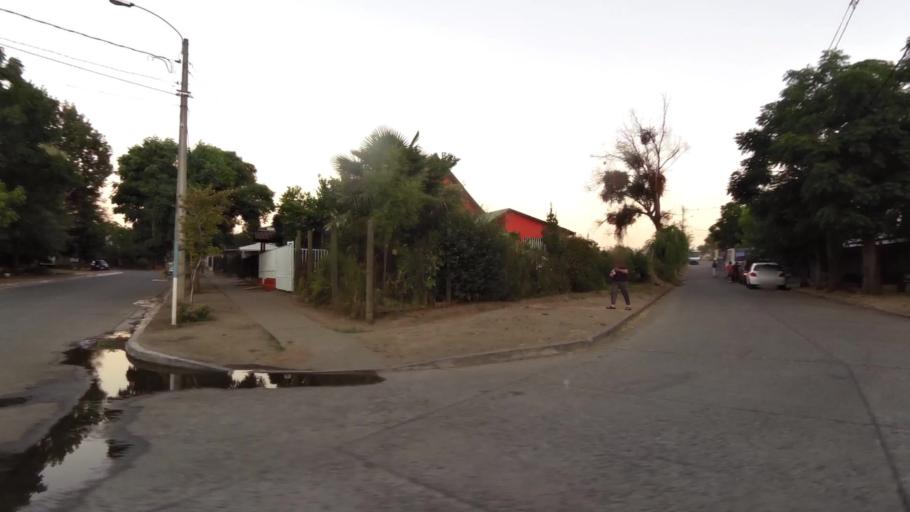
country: CL
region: Maule
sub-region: Provincia de Talca
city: Talca
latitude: -35.4500
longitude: -71.6289
